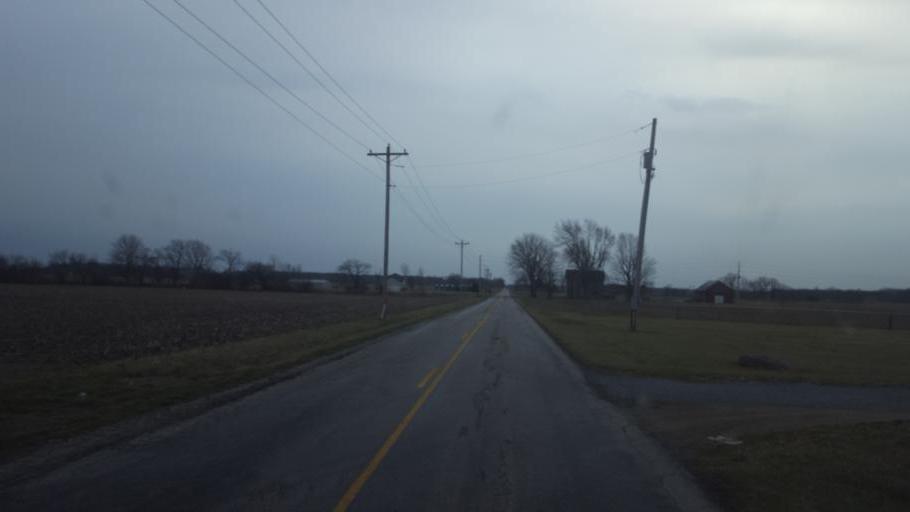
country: US
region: Ohio
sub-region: Marion County
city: Marion
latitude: 40.6523
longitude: -82.9934
